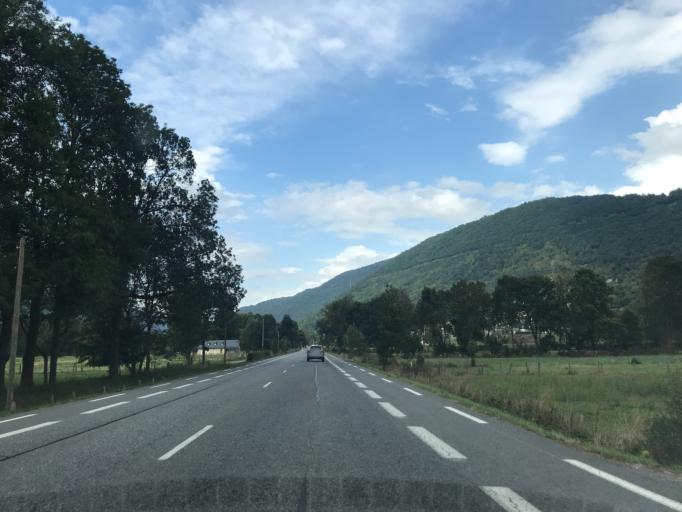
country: FR
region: Midi-Pyrenees
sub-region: Departement des Hautes-Pyrenees
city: Saint-Lary-Soulan
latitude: 42.8417
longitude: 0.3440
